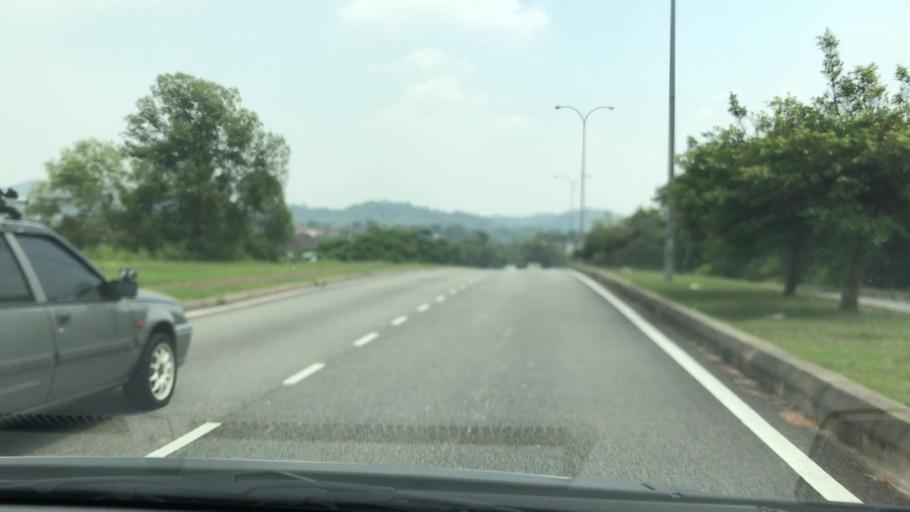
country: MY
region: Putrajaya
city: Putrajaya
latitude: 2.9898
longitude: 101.6639
